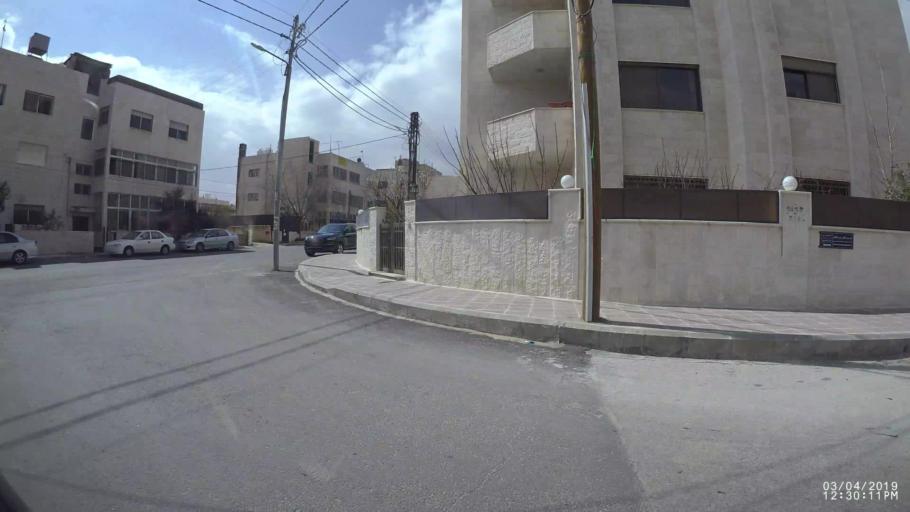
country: JO
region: Amman
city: Wadi as Sir
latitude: 31.9599
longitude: 35.8402
